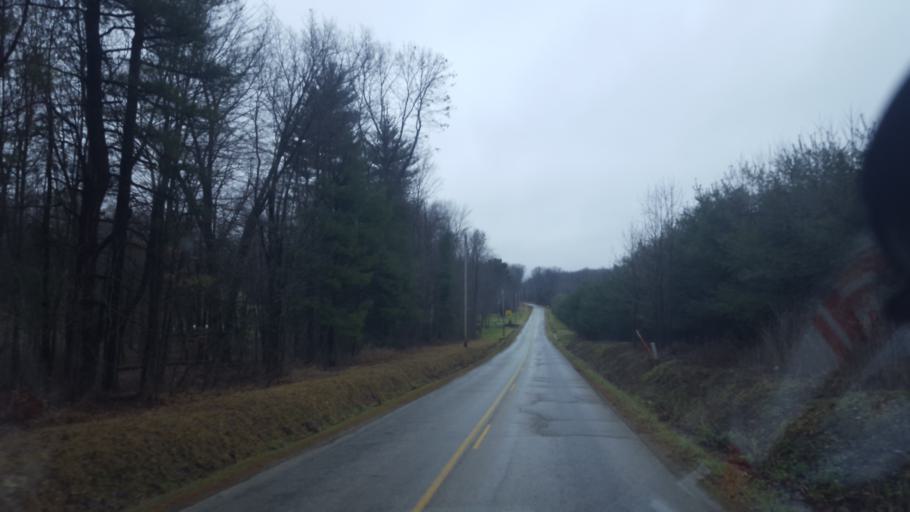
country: US
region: Ohio
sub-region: Ashland County
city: Loudonville
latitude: 40.5672
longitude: -82.3564
